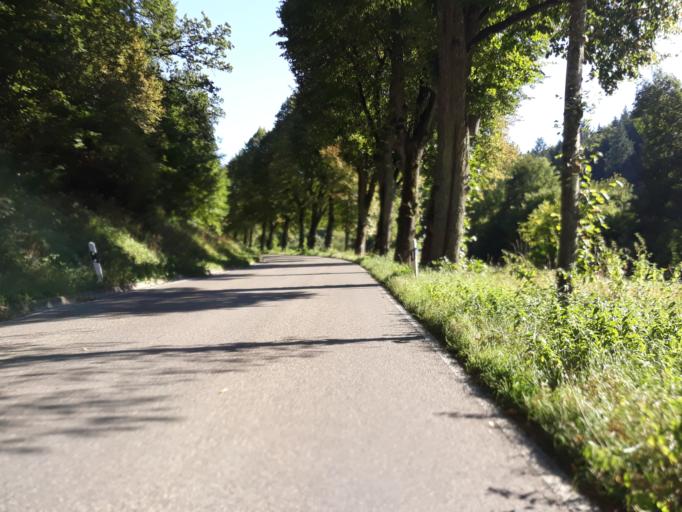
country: DE
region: Baden-Wuerttemberg
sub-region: Regierungsbezirk Stuttgart
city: Aidlingen
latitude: 48.6738
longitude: 8.9117
